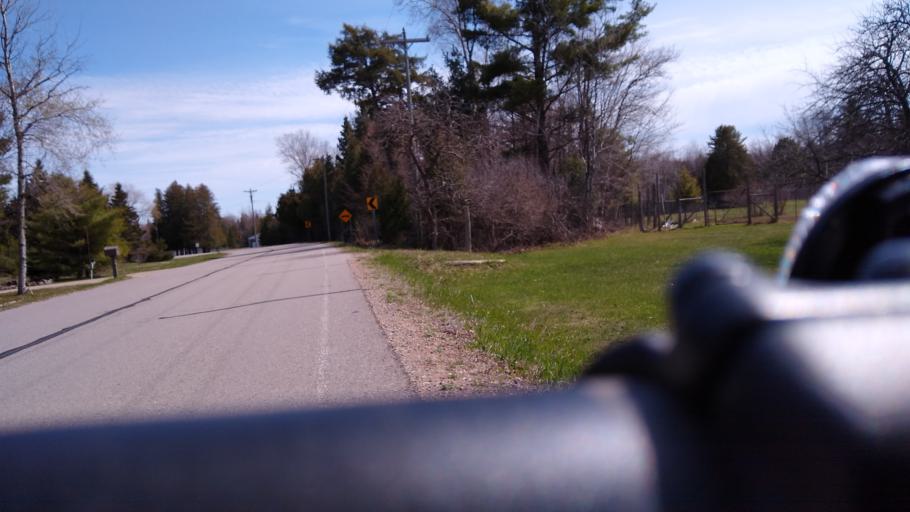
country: US
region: Michigan
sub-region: Delta County
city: Escanaba
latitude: 45.6878
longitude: -87.1525
